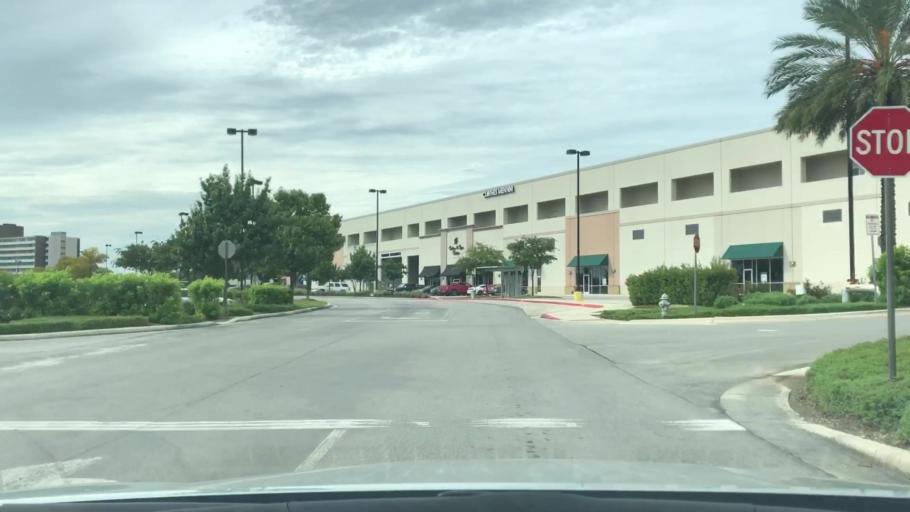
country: US
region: Texas
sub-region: Bexar County
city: Castle Hills
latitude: 29.5175
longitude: -98.5033
